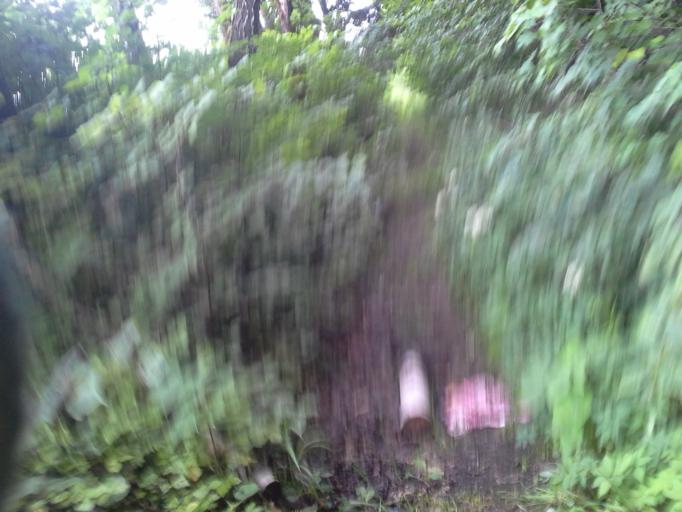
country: RU
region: Moskovskaya
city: Lesnoy Gorodok
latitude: 55.6428
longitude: 37.2427
